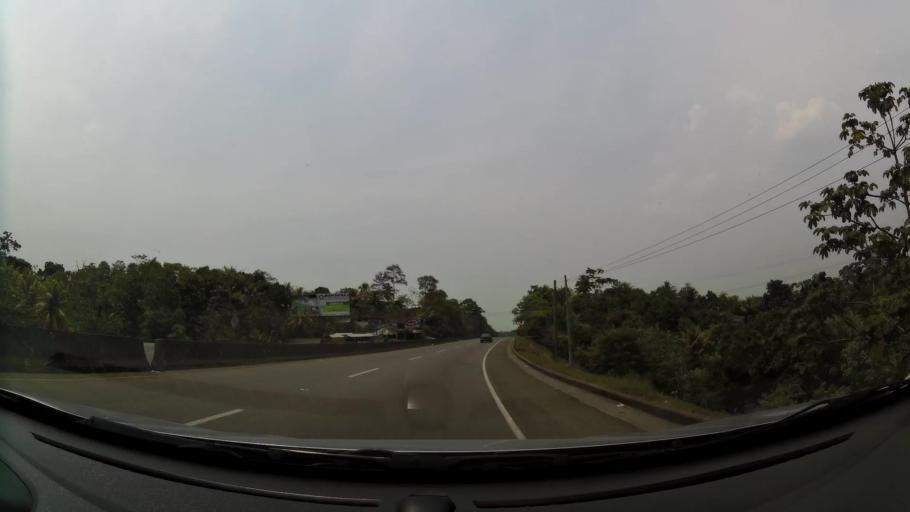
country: HN
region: Cortes
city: Oropendolas
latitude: 14.9920
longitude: -87.9310
